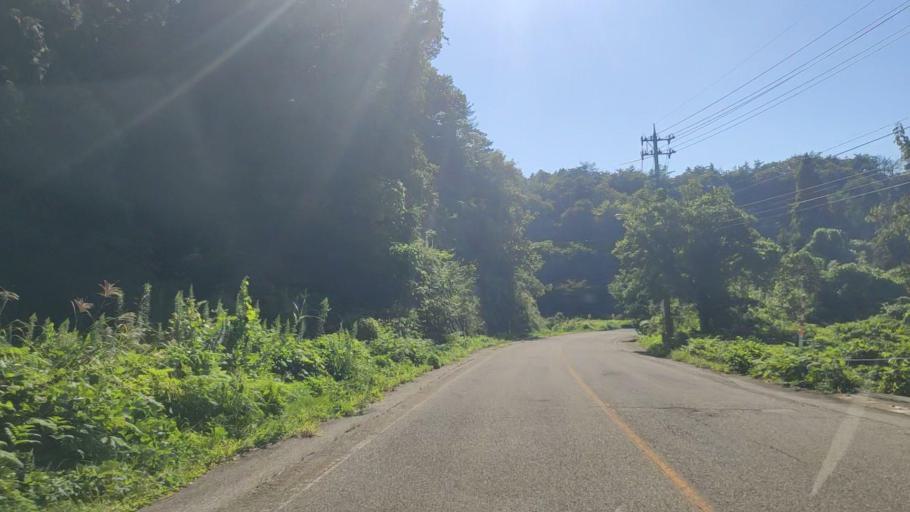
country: JP
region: Ishikawa
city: Nanao
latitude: 37.3158
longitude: 137.1643
